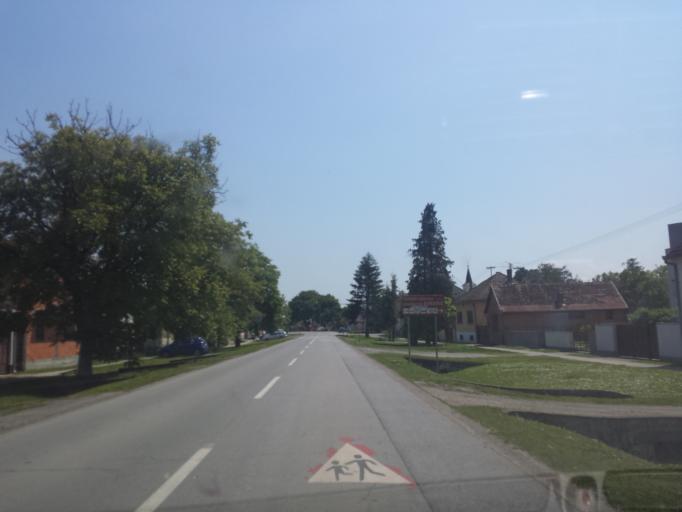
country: HR
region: Brodsko-Posavska
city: Luzani
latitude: 45.1677
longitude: 17.6999
